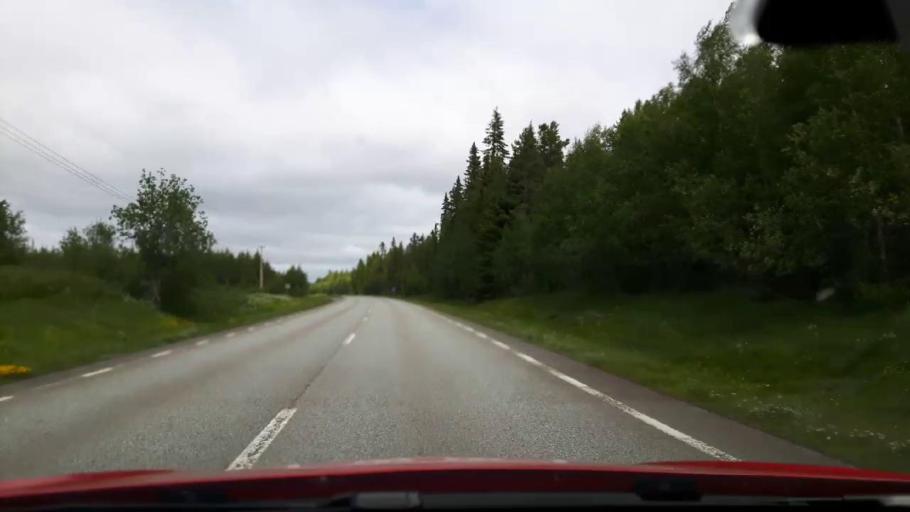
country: SE
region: Jaemtland
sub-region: Krokoms Kommun
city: Krokom
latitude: 63.4771
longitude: 14.5044
